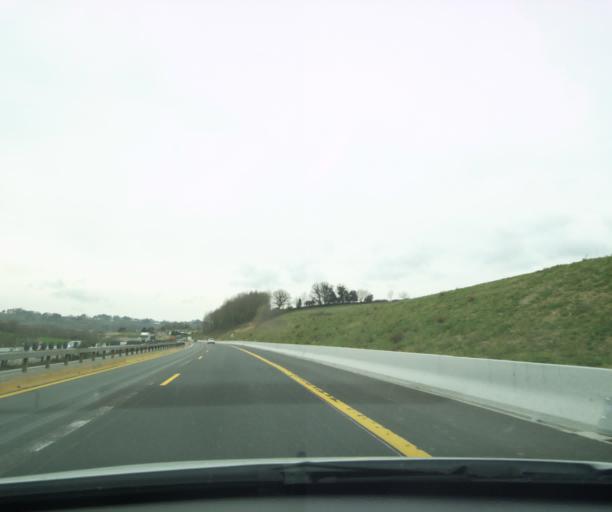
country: FR
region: Aquitaine
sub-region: Departement des Pyrenees-Atlantiques
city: Urrugne
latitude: 43.3586
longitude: -1.7093
